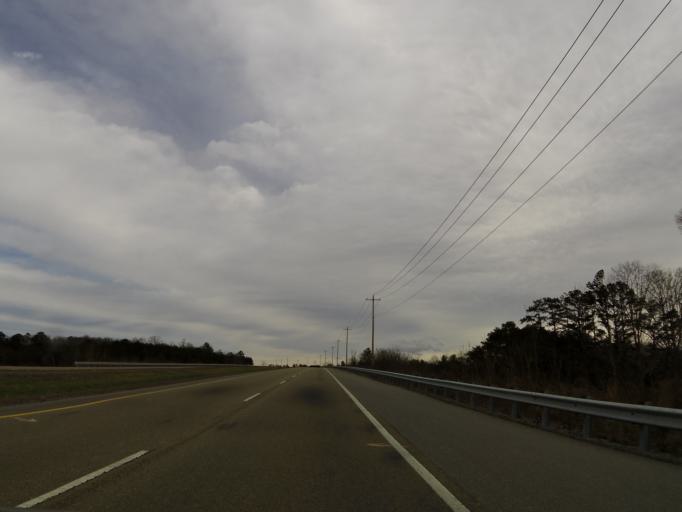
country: US
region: Tennessee
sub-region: Cocke County
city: Newport
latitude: 35.9931
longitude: -83.1139
